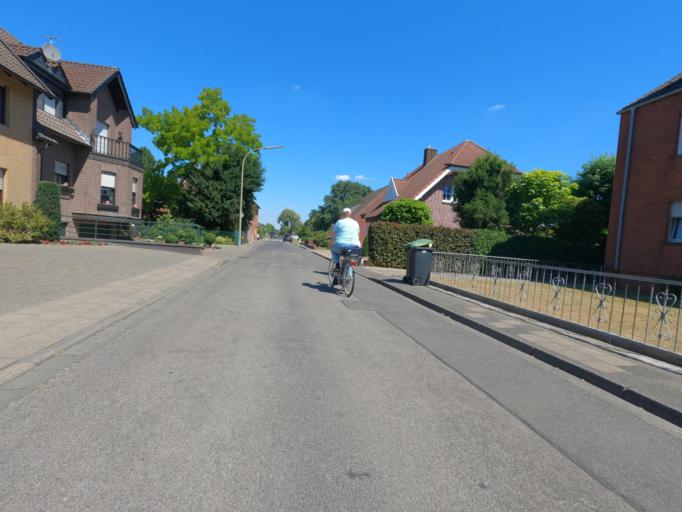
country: DE
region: North Rhine-Westphalia
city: Wegberg
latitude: 51.1340
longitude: 6.3085
